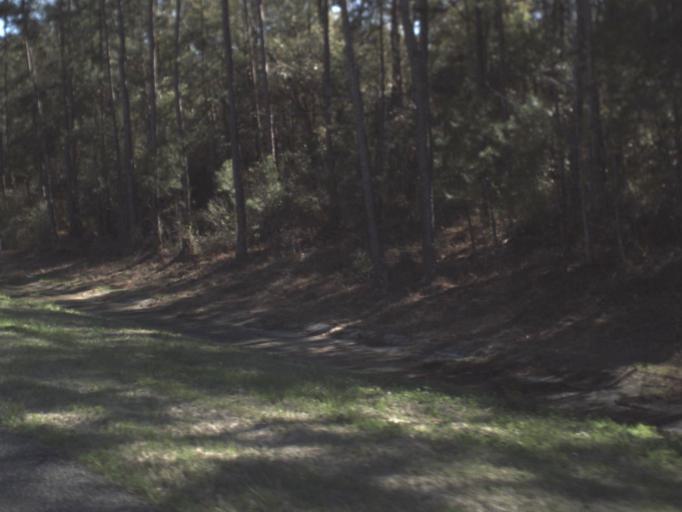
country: US
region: Florida
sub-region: Gadsden County
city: Midway
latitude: 30.5117
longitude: -84.4578
